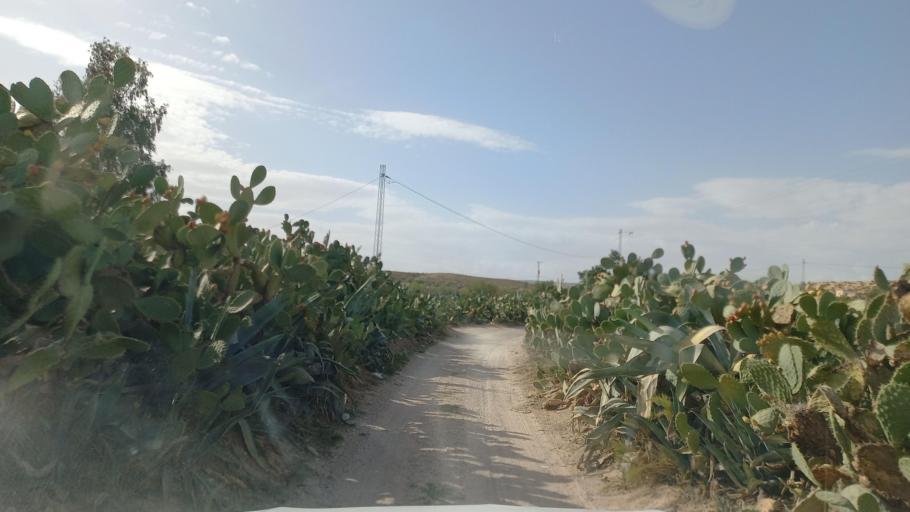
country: TN
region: Al Qasrayn
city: Kasserine
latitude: 35.2547
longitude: 8.9311
